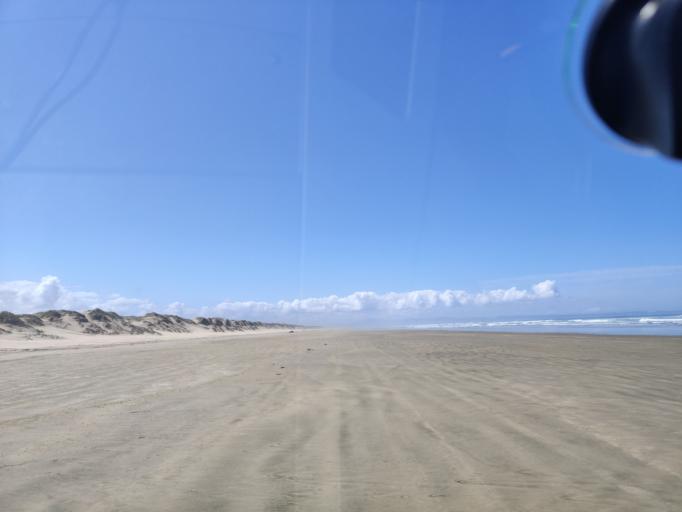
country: NZ
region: Northland
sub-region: Far North District
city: Kaitaia
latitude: -34.9361
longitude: 173.1122
